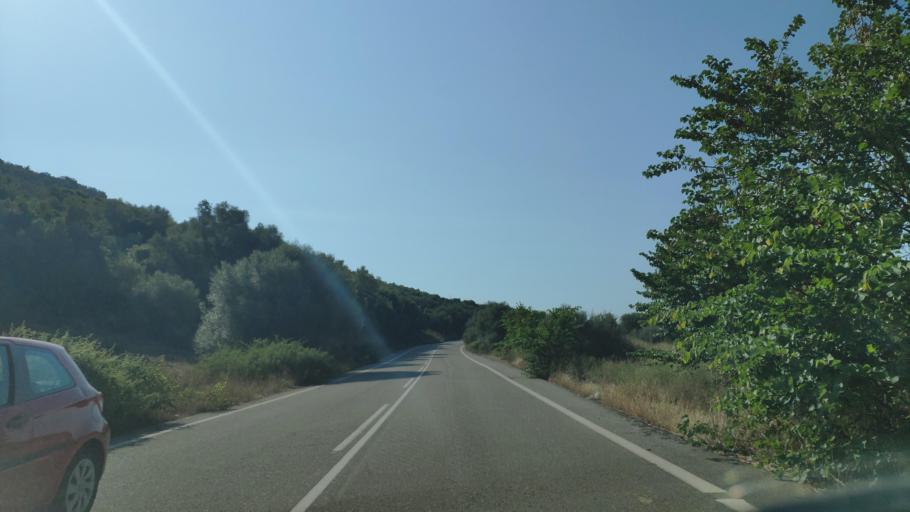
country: GR
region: West Greece
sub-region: Nomos Aitolias kai Akarnanias
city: Stanos
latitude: 38.7737
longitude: 21.1538
